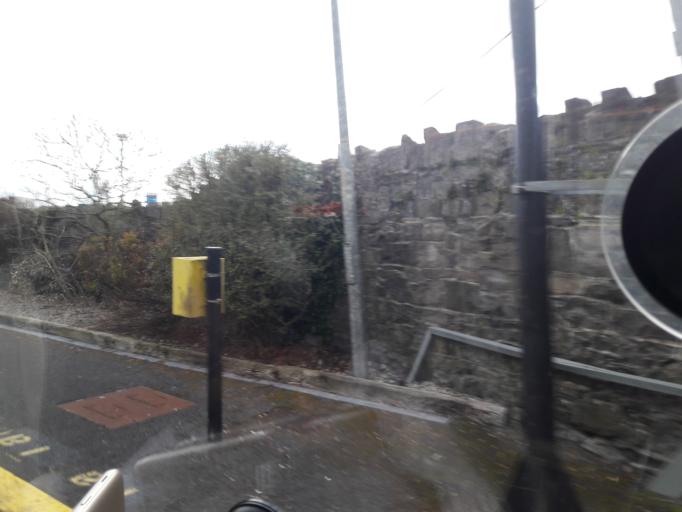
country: IE
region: Leinster
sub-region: An Iarmhi
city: An Muileann gCearr
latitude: 53.5235
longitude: -7.3470
